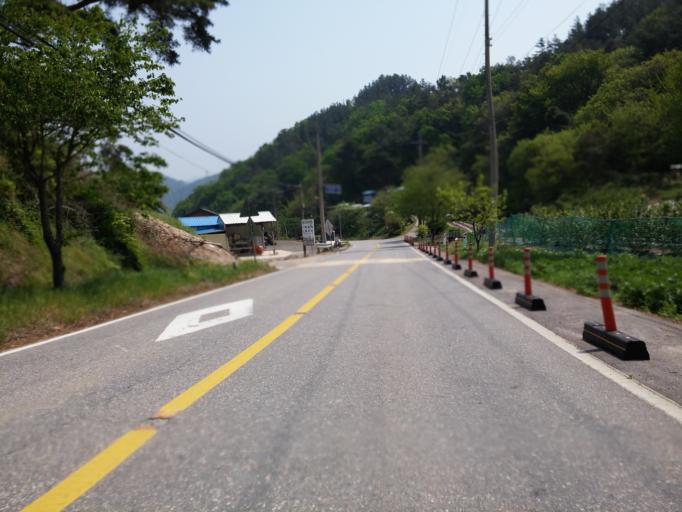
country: KR
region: Daejeon
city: Sintansin
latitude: 36.4312
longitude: 127.5423
